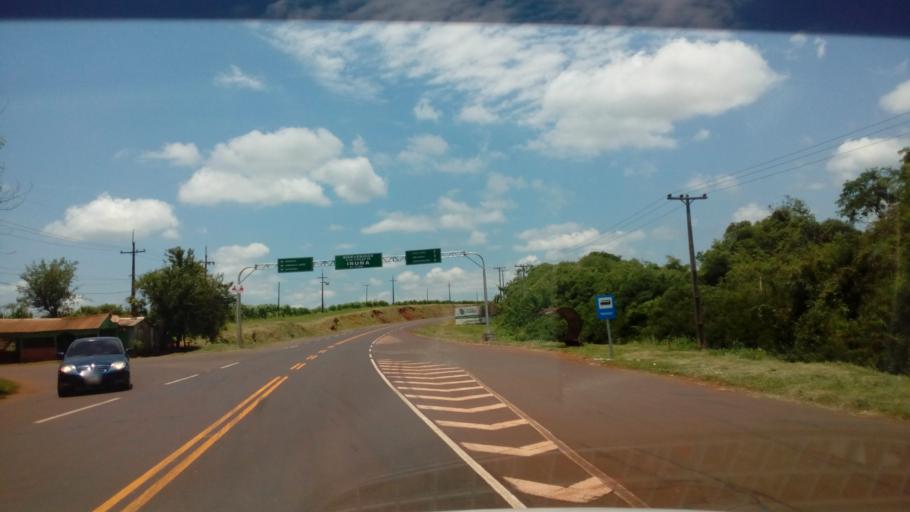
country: PY
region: Alto Parana
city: Naranjal
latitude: -26.0489
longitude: -55.1298
